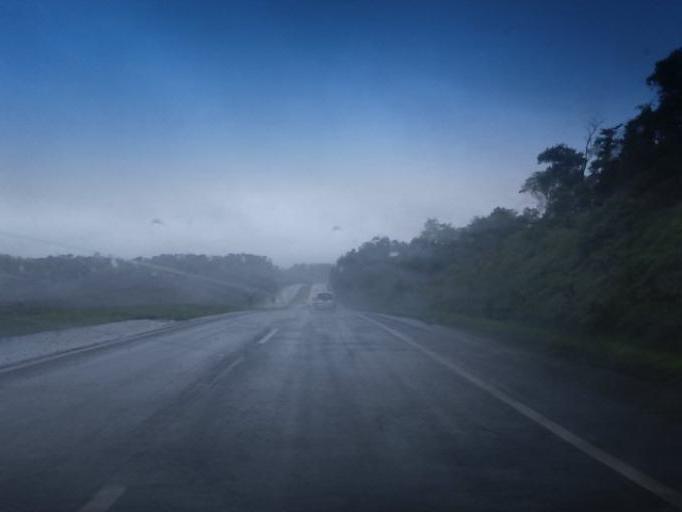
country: BR
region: Parana
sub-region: Antonina
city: Antonina
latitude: -25.1044
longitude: -48.7119
